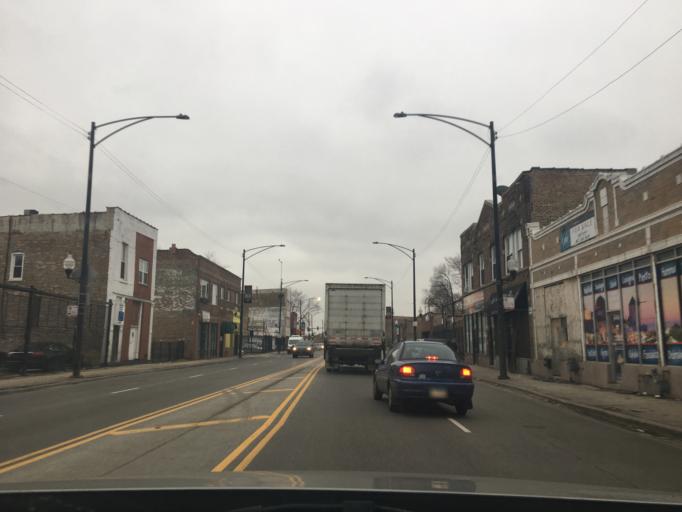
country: US
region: Illinois
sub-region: Cook County
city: Oak Park
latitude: 41.8930
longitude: -87.7458
